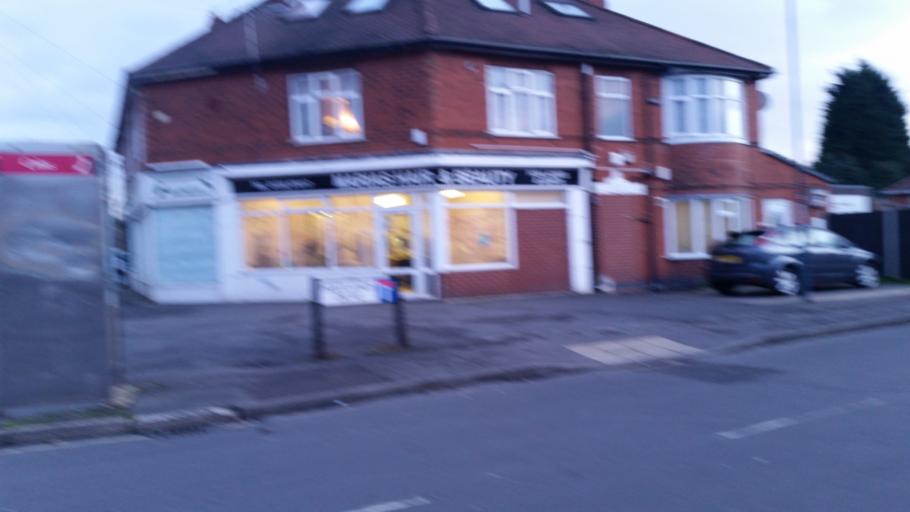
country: GB
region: England
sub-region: Derby
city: Derby
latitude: 52.8900
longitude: -1.4418
